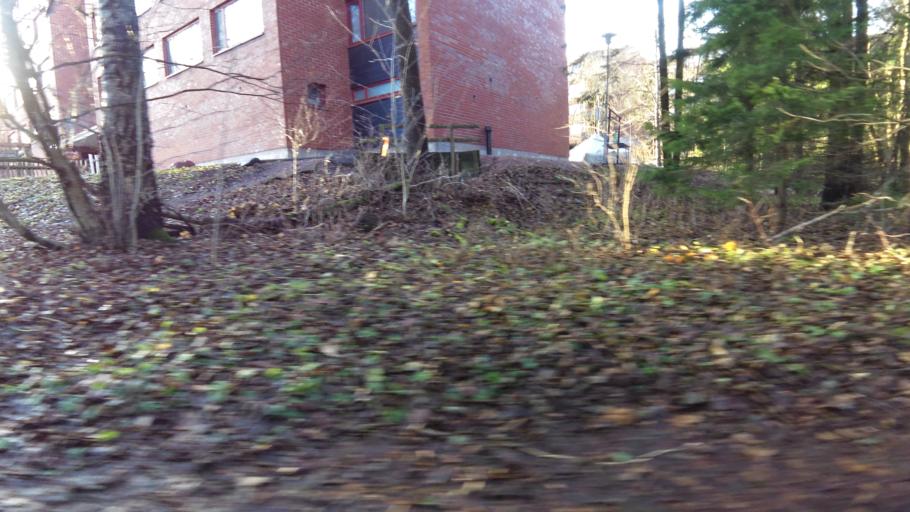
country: FI
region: Uusimaa
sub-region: Helsinki
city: Teekkarikylae
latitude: 60.1907
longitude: 24.8402
